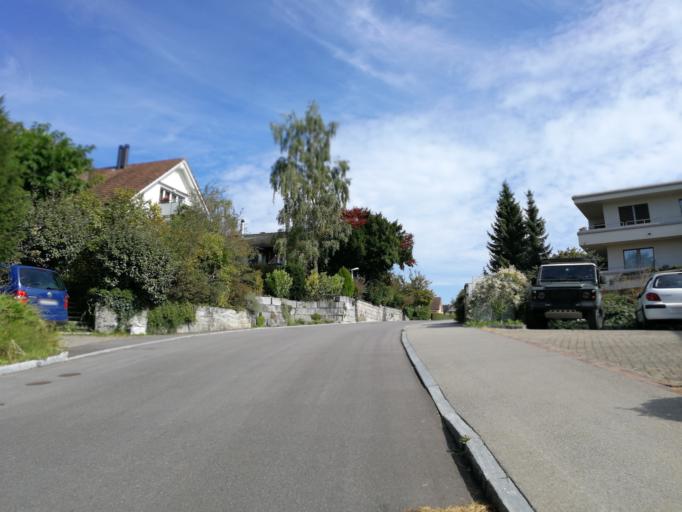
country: CH
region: Zurich
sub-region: Bezirk Meilen
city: Obermeilen
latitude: 47.2637
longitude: 8.6667
